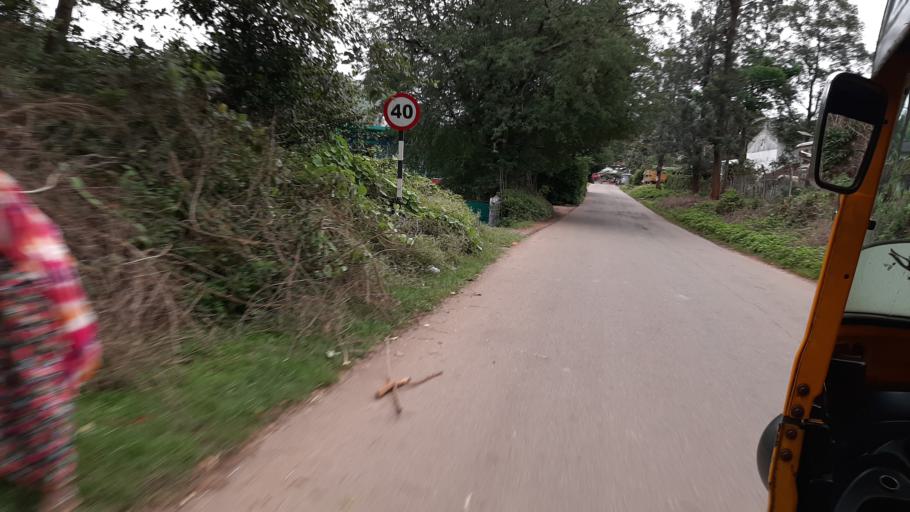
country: IN
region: Andhra Pradesh
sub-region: Vizianagaram District
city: Salur
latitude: 18.2378
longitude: 83.0024
